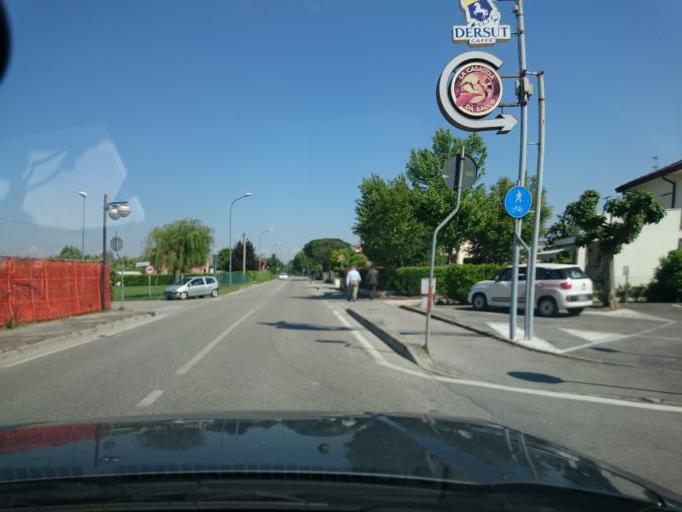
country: IT
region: Veneto
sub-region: Provincia di Venezia
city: Stra
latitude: 45.4178
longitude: 12.0160
